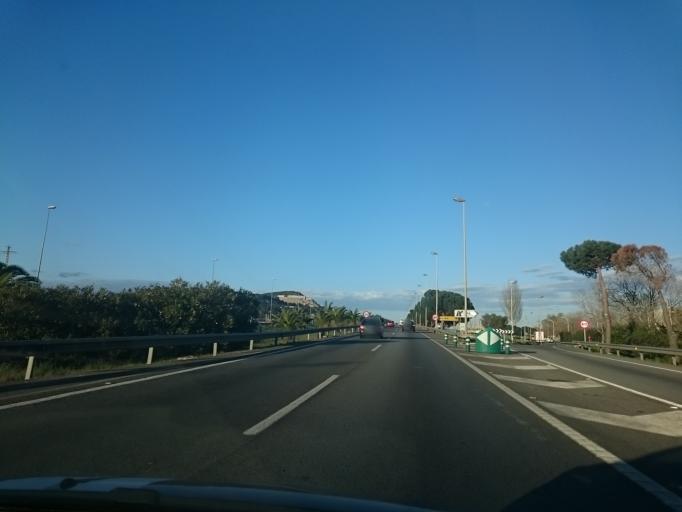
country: ES
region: Catalonia
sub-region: Provincia de Barcelona
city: Sants-Montjuic
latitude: 41.3470
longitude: 2.1419
